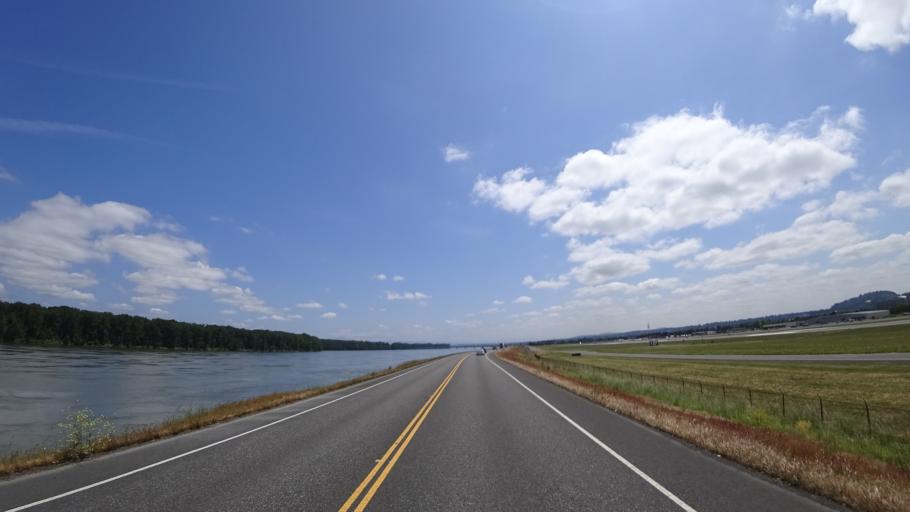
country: US
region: Washington
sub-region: Clark County
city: Orchards
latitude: 45.5884
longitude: -122.5732
